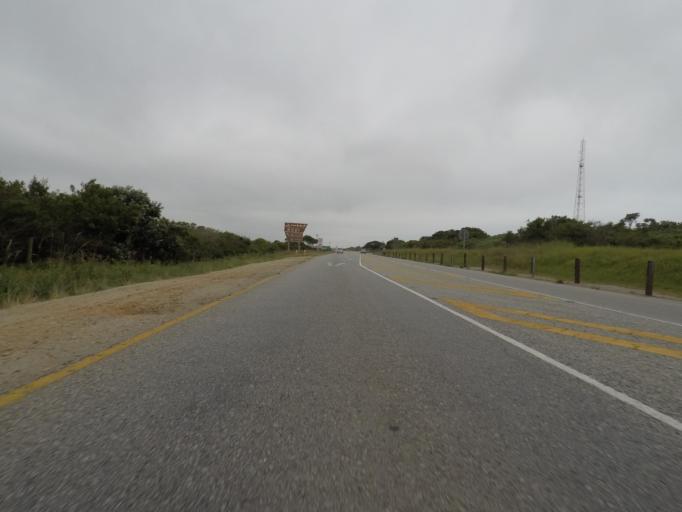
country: ZA
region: Eastern Cape
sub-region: Cacadu District Municipality
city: Port Alfred
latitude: -33.6796
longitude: 26.6650
